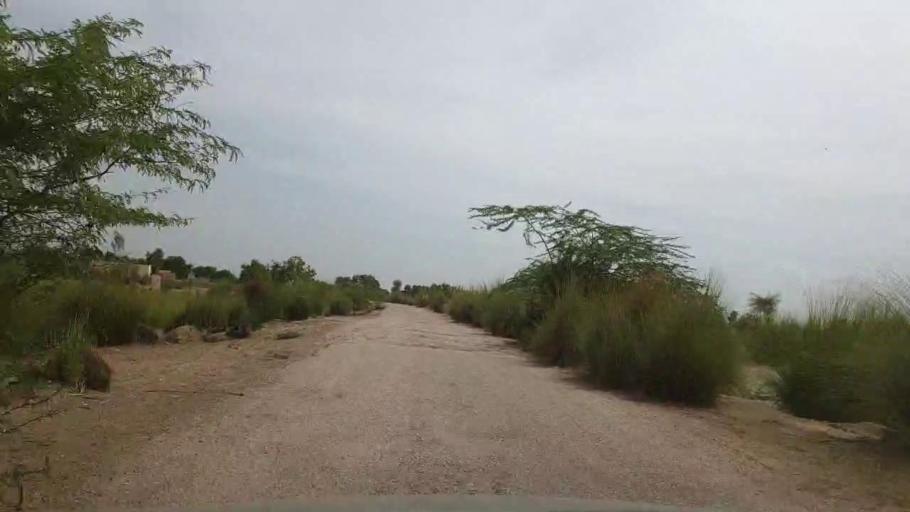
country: PK
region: Sindh
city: Bozdar
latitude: 27.0920
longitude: 69.0149
